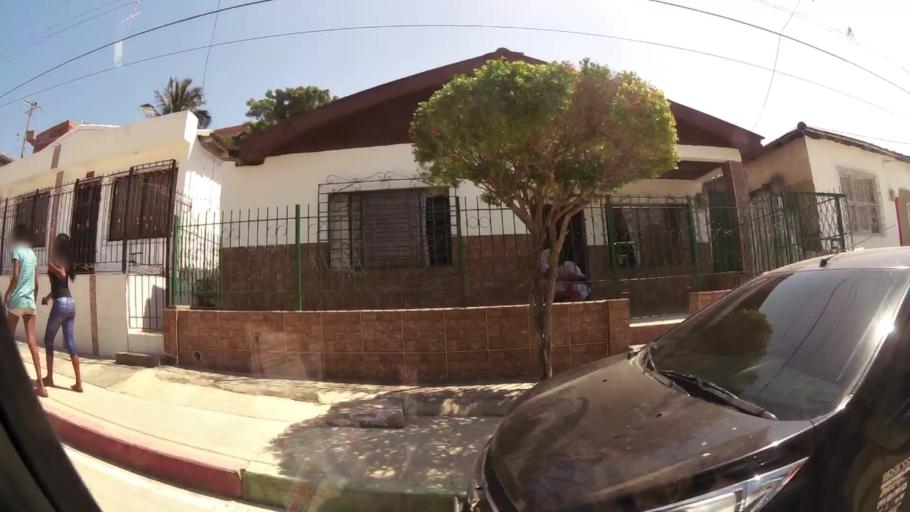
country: CO
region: Bolivar
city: Cartagena
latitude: 10.4335
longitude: -75.5278
